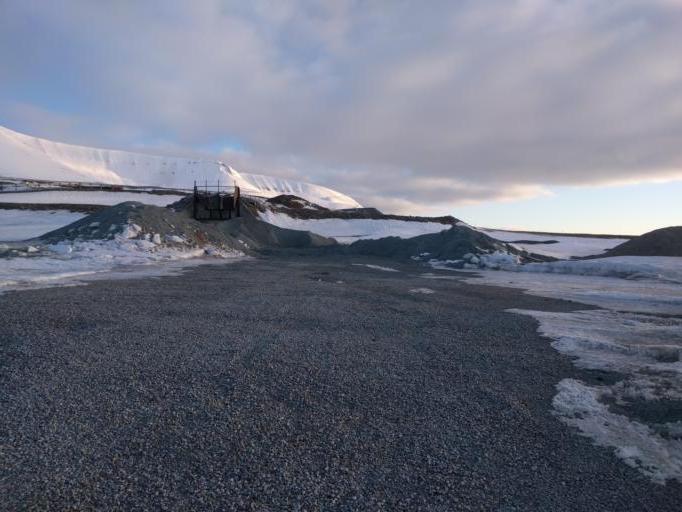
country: SJ
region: Svalbard
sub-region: Spitsbergen
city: Longyearbyen
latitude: 78.2404
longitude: 15.5121
